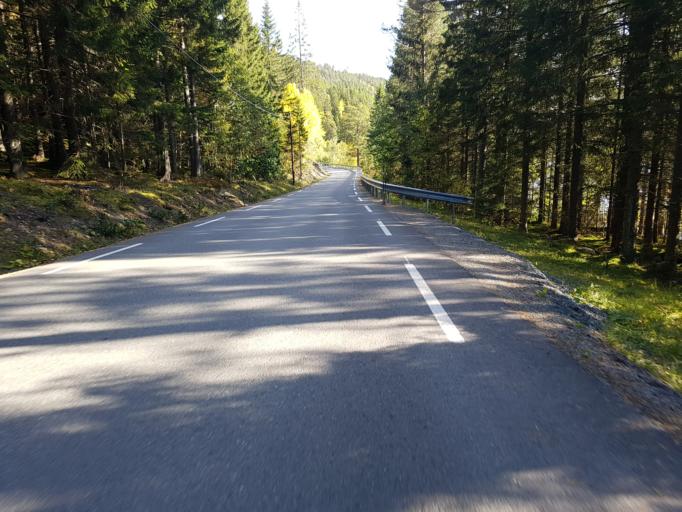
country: NO
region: Sor-Trondelag
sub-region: Malvik
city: Malvik
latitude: 63.3761
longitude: 10.6068
